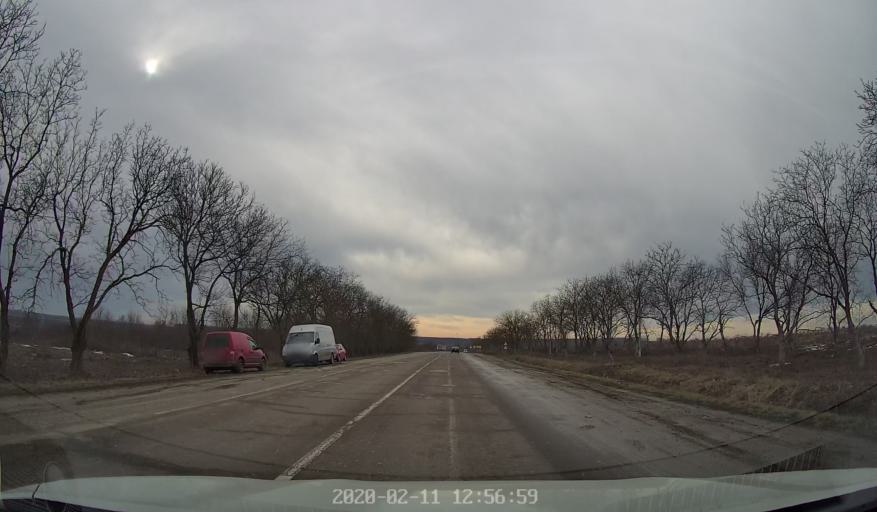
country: MD
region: Briceni
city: Briceni
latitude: 48.3454
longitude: 27.0725
